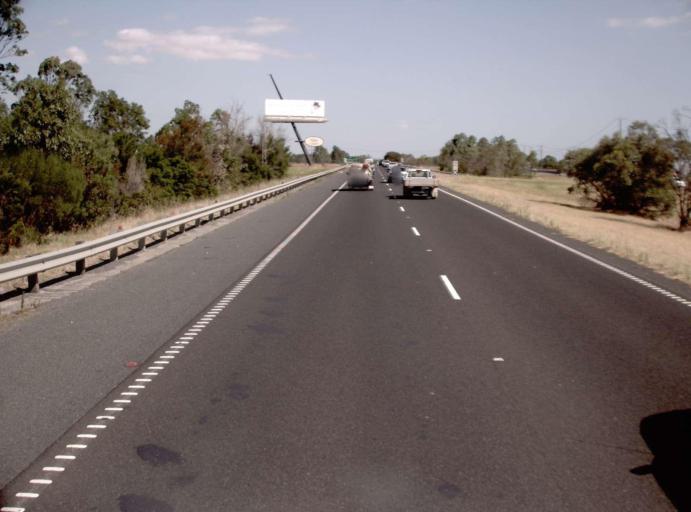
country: AU
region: Victoria
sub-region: Kingston
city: Patterson Lakes
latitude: -38.0559
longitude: 145.1465
